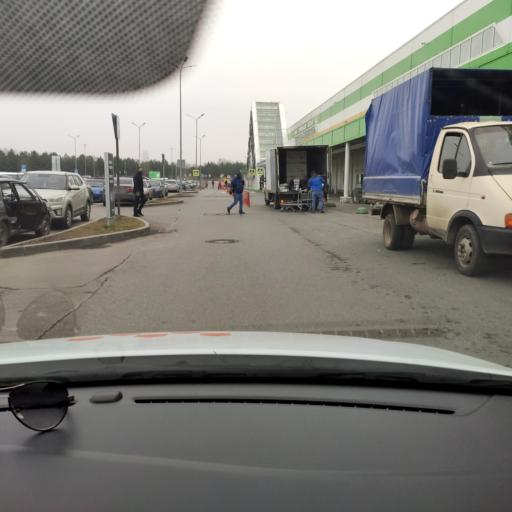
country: RU
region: Tatarstan
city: Stolbishchi
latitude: 55.7255
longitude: 49.1993
